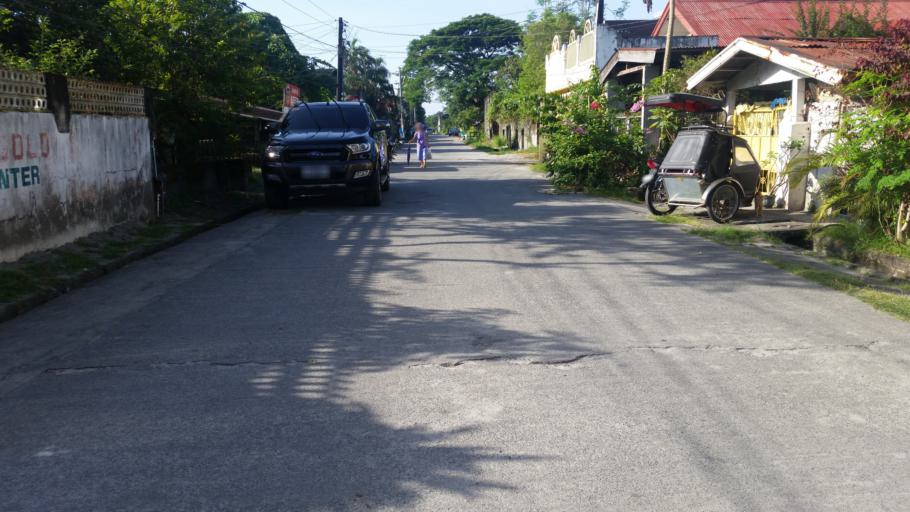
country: PH
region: Central Luzon
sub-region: Province of Pampanga
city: Mabalacat City
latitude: 15.2760
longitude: 120.5682
